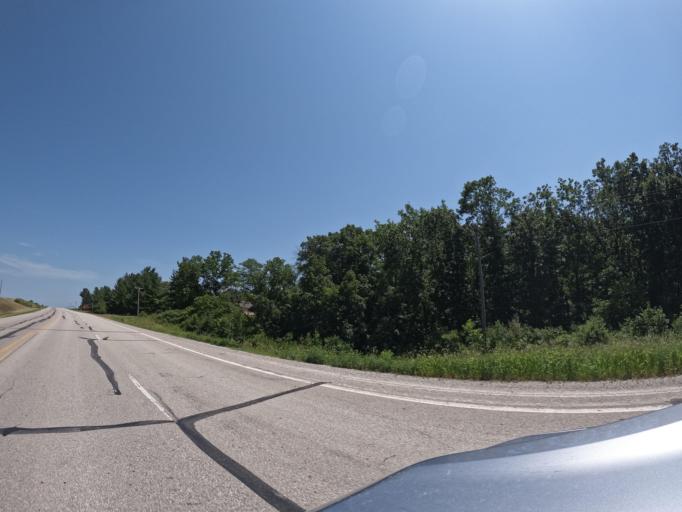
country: US
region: Iowa
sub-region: Henry County
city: Mount Pleasant
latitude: 40.9671
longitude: -91.6263
